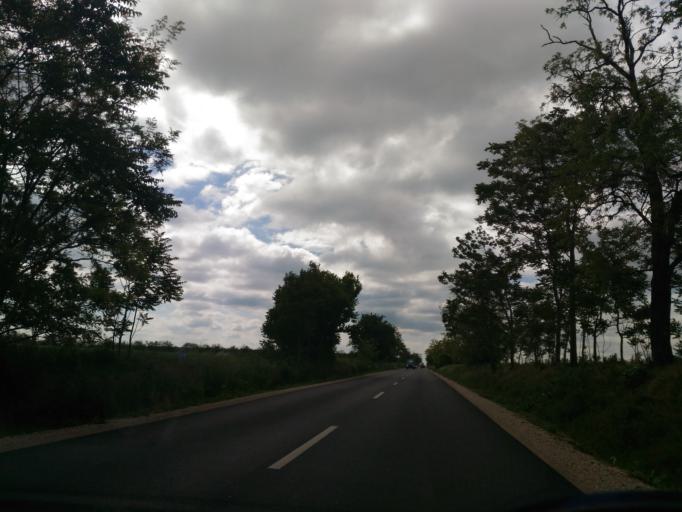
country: HU
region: Fejer
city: Kapolnasnyek
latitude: 47.2119
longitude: 18.6840
